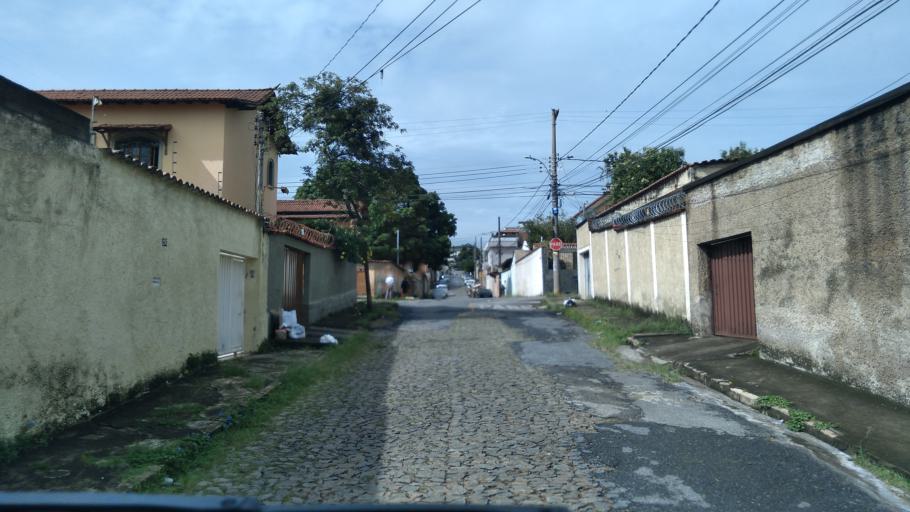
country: BR
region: Minas Gerais
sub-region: Contagem
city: Contagem
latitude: -19.9281
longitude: -43.9994
